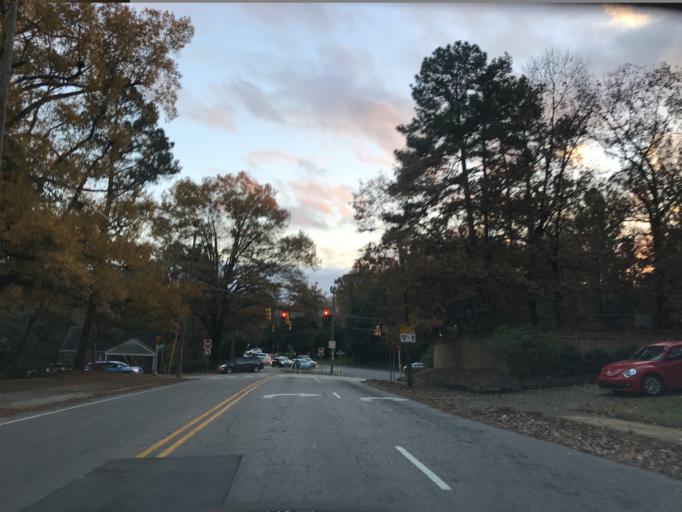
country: US
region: North Carolina
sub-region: Wake County
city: West Raleigh
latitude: 35.8137
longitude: -78.6511
